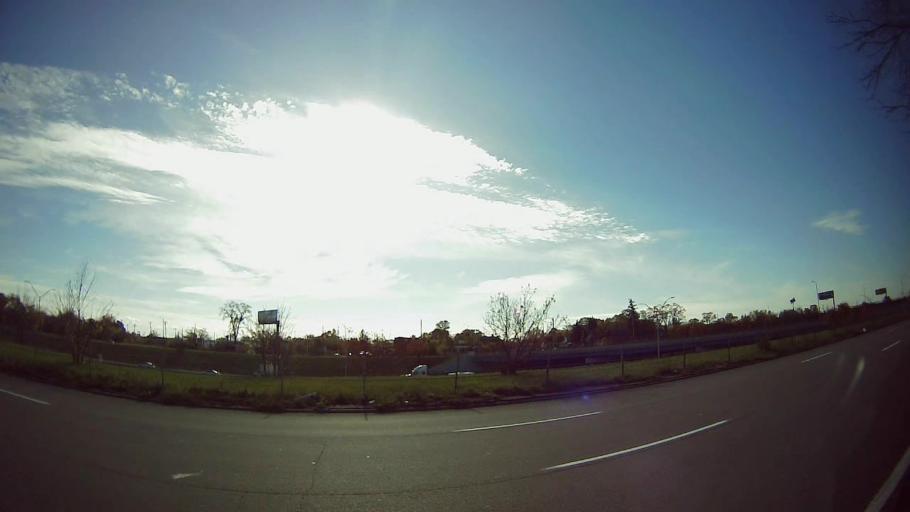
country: US
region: Michigan
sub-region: Wayne County
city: Dearborn
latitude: 42.3846
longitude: -83.1753
